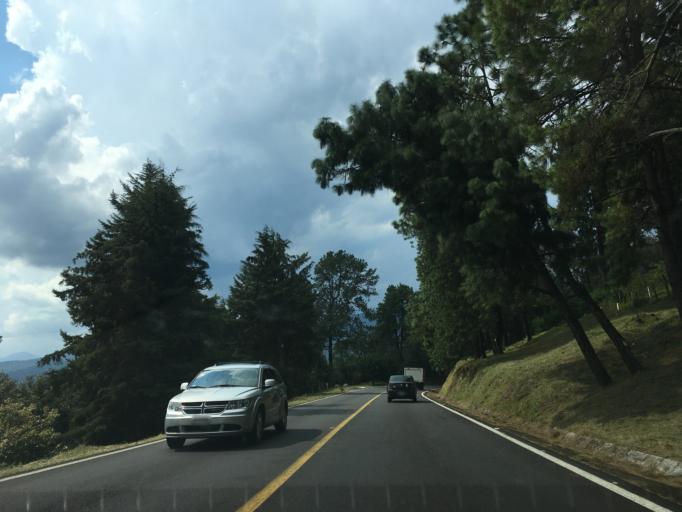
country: MX
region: Michoacan
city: Tingambato
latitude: 19.4953
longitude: -101.8368
